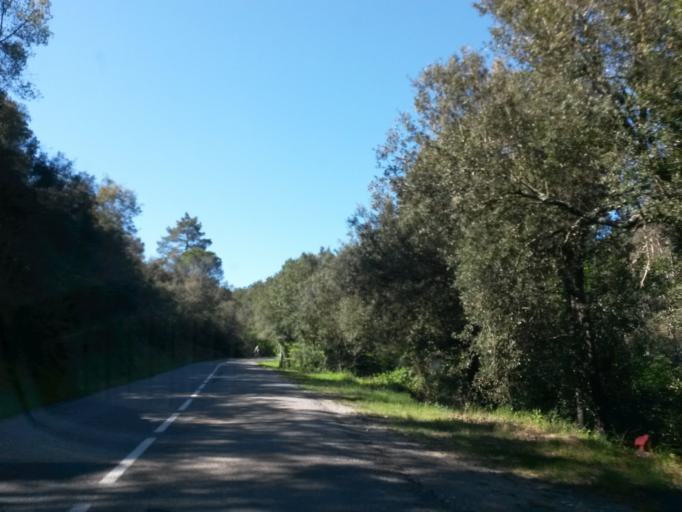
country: ES
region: Catalonia
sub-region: Provincia de Girona
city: Madremanya
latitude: 41.9842
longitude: 2.9479
